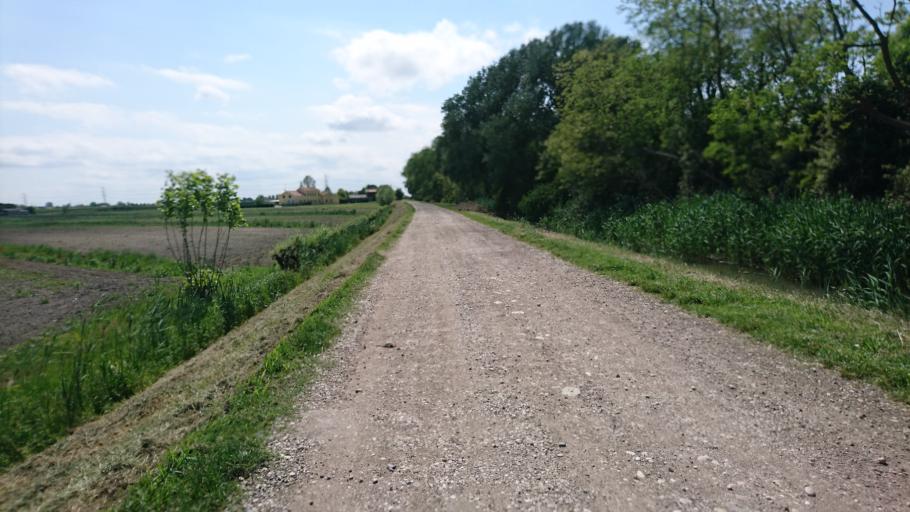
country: IT
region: Veneto
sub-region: Provincia di Padova
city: Codevigo
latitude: 45.2577
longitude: 12.1377
